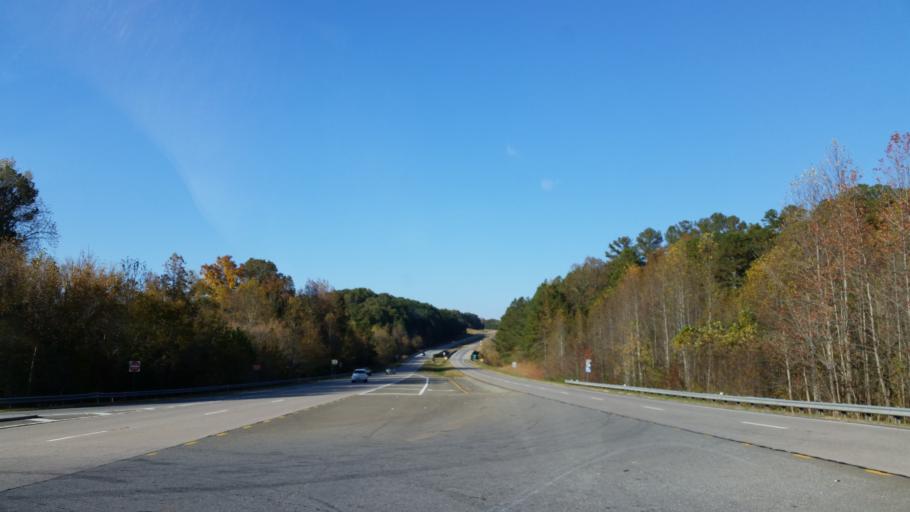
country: US
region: Georgia
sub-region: Pickens County
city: Jasper
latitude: 34.5177
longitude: -84.5189
